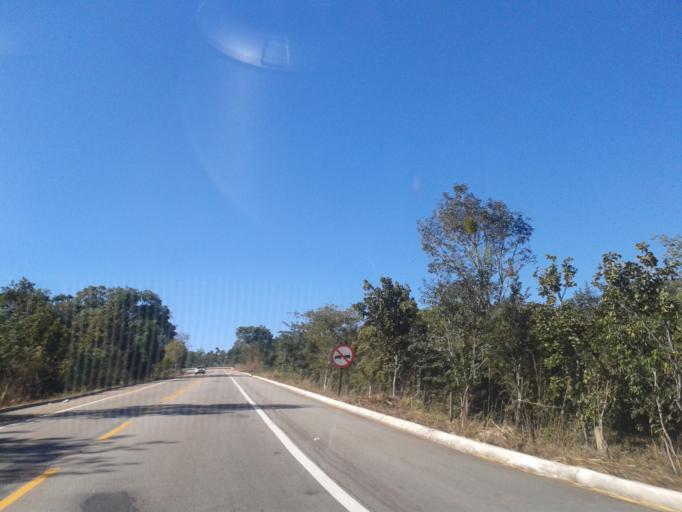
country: BR
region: Goias
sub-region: Goias
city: Goias
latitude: -15.8712
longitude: -50.0911
